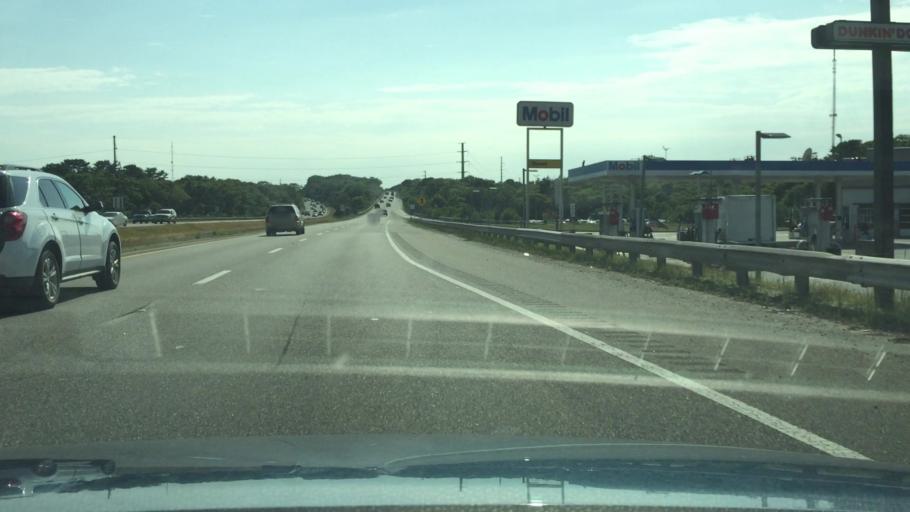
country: US
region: Massachusetts
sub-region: Barnstable County
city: Barnstable
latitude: 41.6874
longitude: -70.3369
